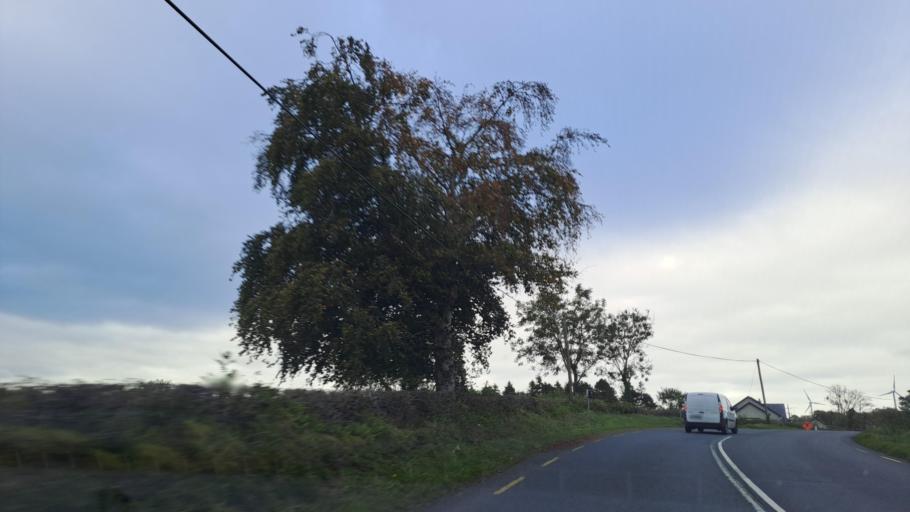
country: IE
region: Ulster
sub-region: An Cabhan
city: Cootehill
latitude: 54.0676
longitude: -6.9362
